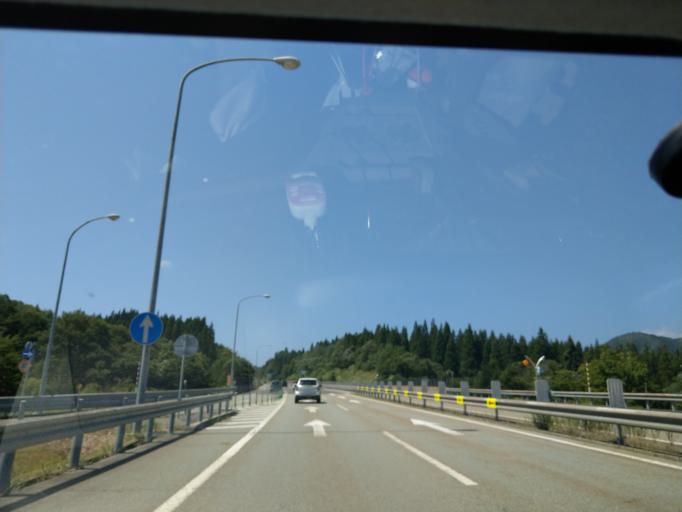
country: JP
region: Akita
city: Omagari
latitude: 39.4265
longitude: 140.4260
